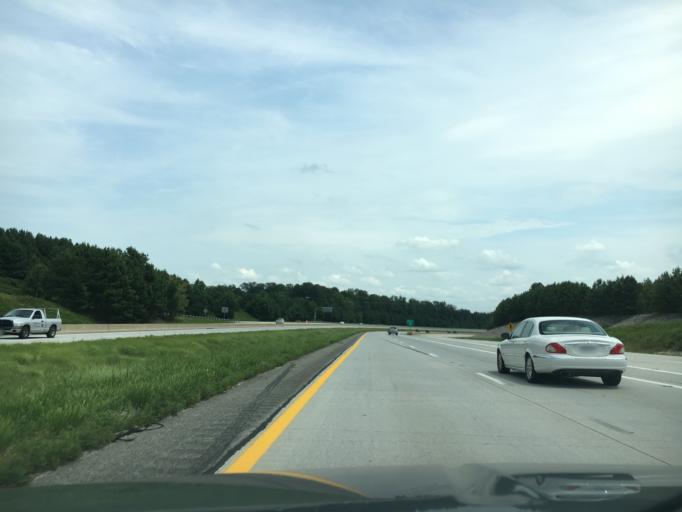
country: US
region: Virginia
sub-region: Chesterfield County
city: Brandermill
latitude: 37.4690
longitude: -77.6467
